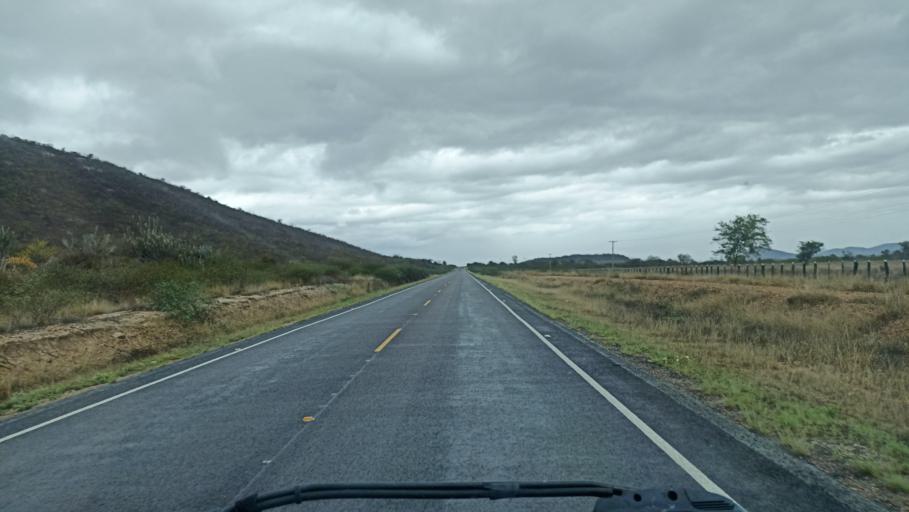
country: BR
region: Bahia
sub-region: Iacu
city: Iacu
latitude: -12.9565
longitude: -40.4686
